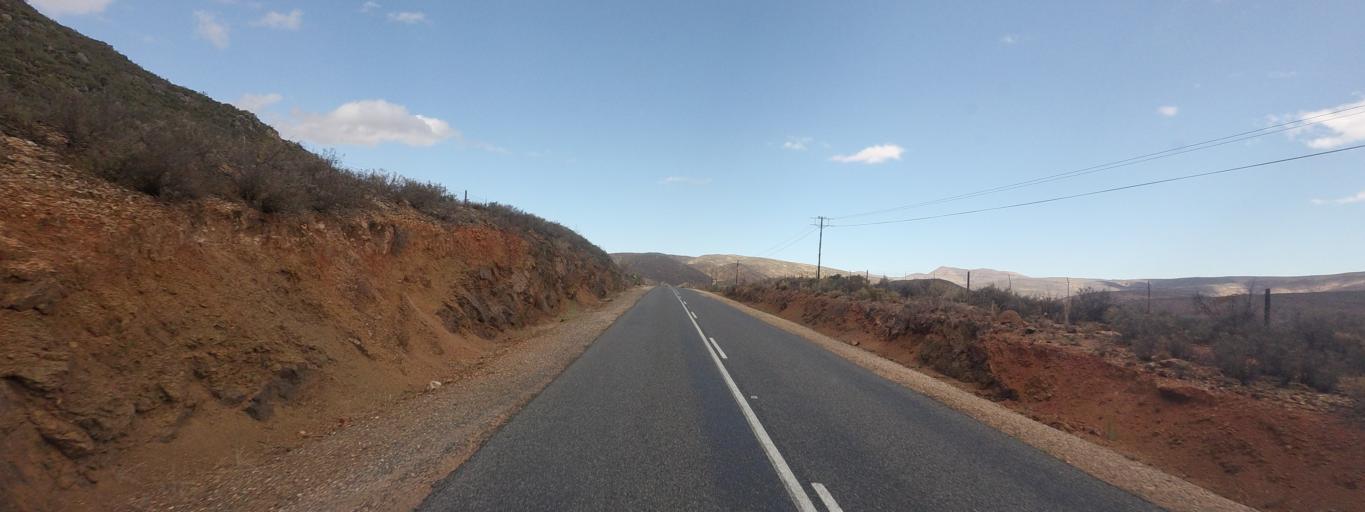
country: ZA
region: Western Cape
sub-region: Eden District Municipality
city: Ladismith
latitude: -33.4726
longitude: 21.4989
